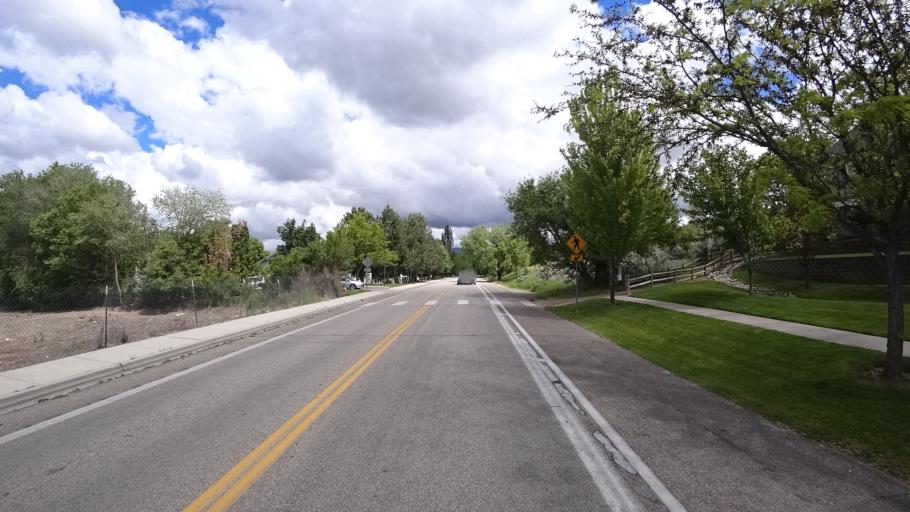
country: US
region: Idaho
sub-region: Ada County
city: Boise
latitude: 43.6405
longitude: -116.2058
